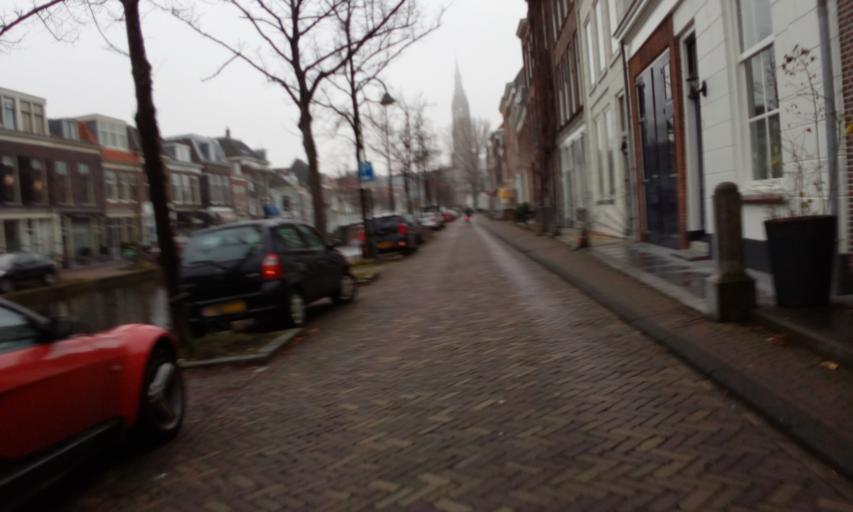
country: NL
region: South Holland
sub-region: Gemeente Delft
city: Delft
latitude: 52.0155
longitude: 4.3561
